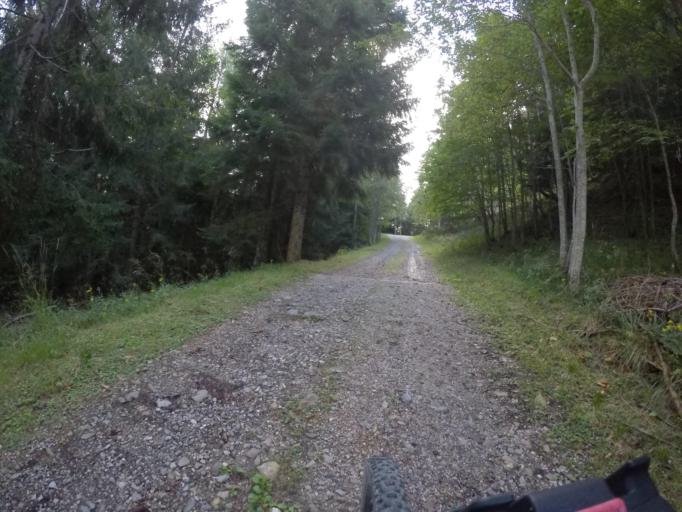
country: IT
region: Friuli Venezia Giulia
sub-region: Provincia di Udine
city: Paularo
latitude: 46.4986
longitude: 13.1815
